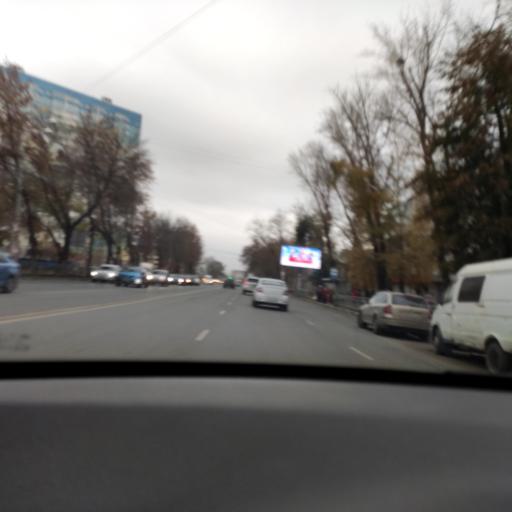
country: RU
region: Samara
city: Samara
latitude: 53.2059
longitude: 50.1899
